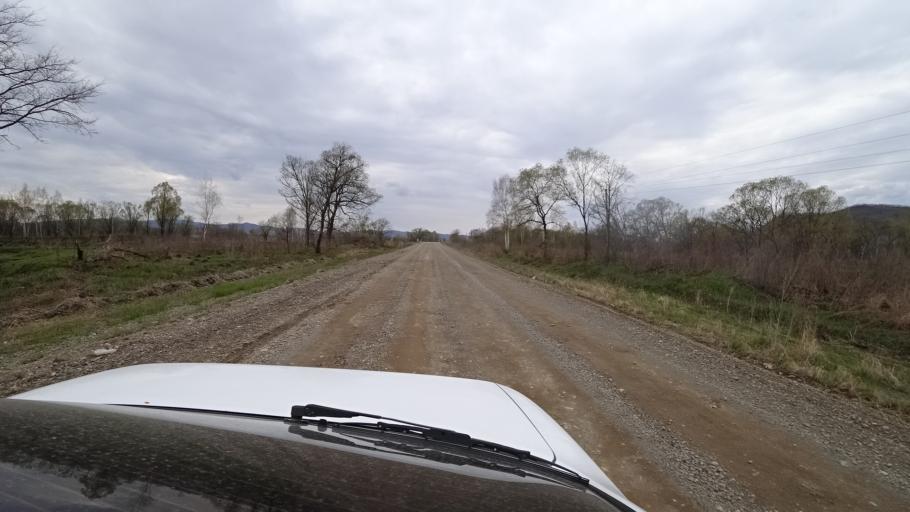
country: RU
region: Primorskiy
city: Novopokrovka
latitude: 45.5618
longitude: 134.3359
